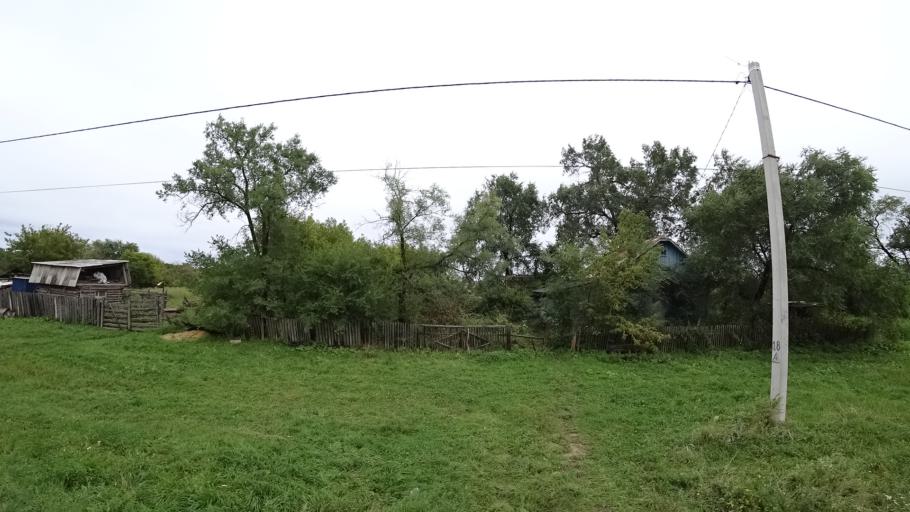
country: RU
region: Primorskiy
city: Monastyrishche
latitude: 44.0799
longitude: 132.5861
